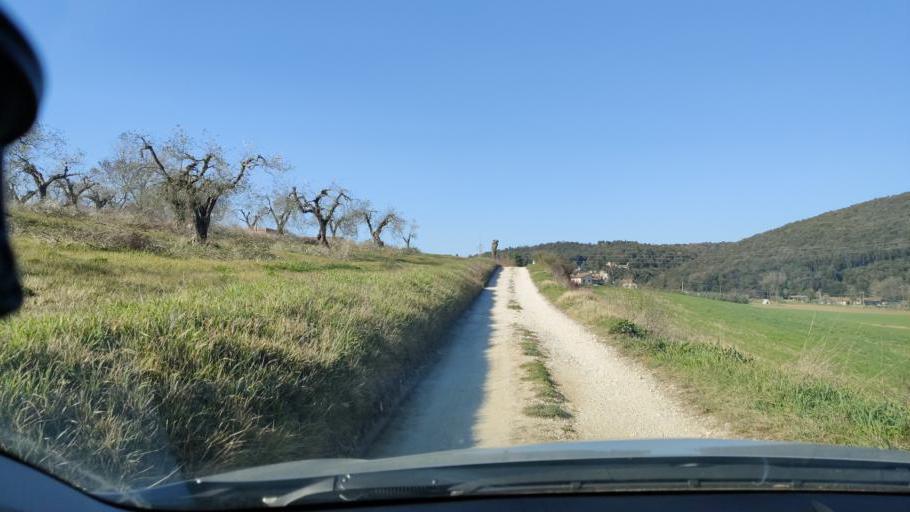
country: IT
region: Umbria
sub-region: Provincia di Terni
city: Fornole
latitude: 42.5594
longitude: 12.4497
